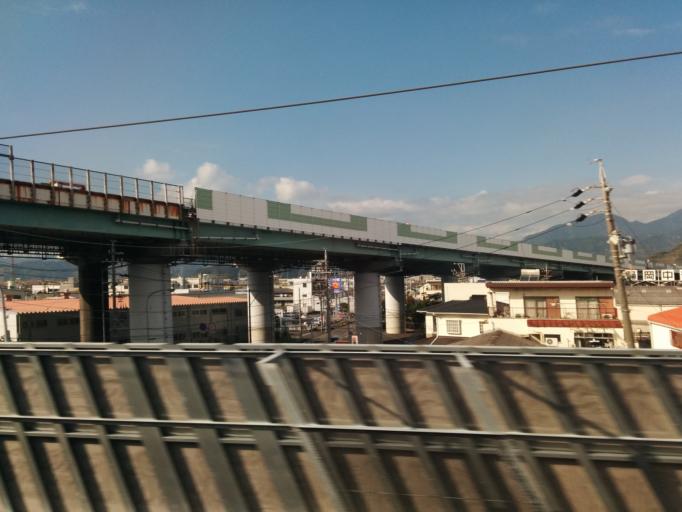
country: JP
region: Shizuoka
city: Shizuoka-shi
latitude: 34.9987
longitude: 138.4348
